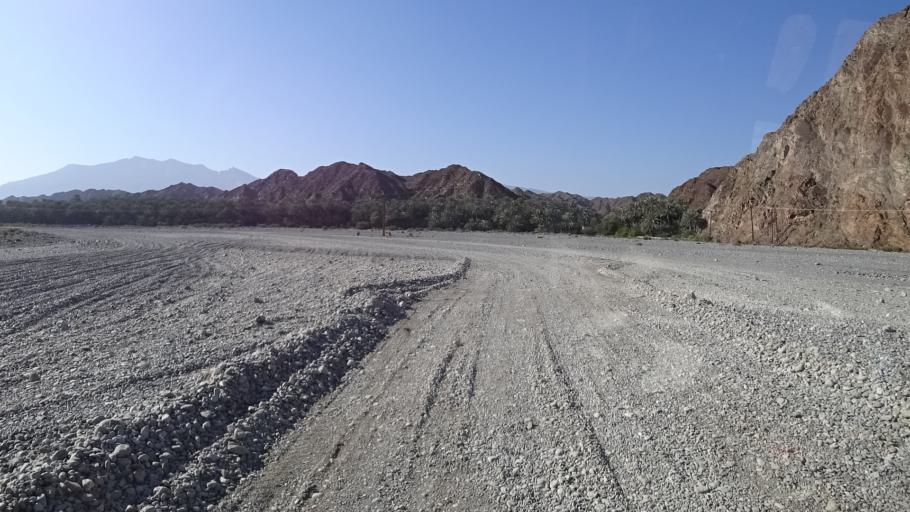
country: OM
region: Al Batinah
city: Bayt al `Awabi
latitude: 23.3883
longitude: 57.6592
